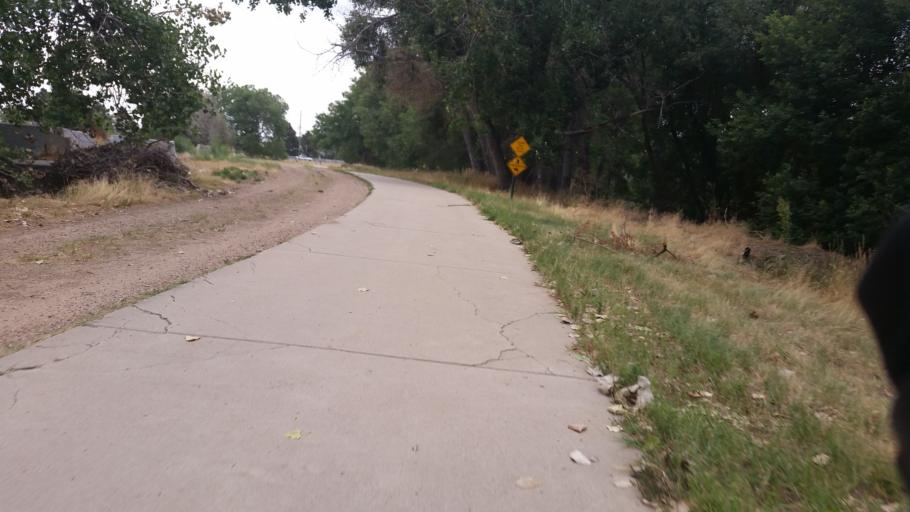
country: US
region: Colorado
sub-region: Adams County
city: Twin Lakes
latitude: 39.8200
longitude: -104.9900
